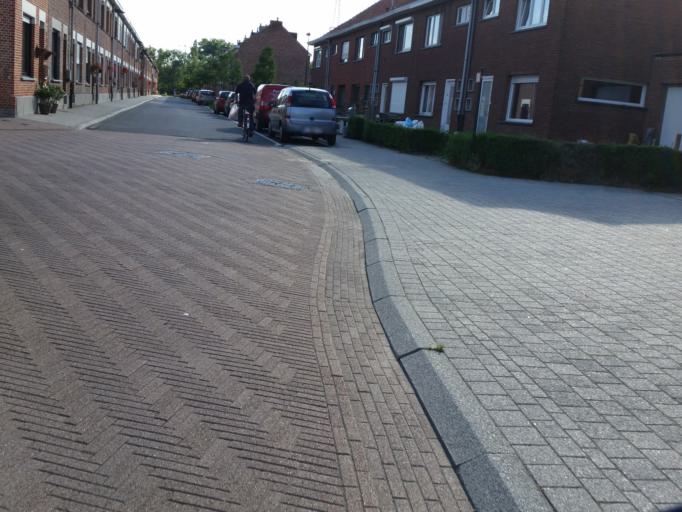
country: BE
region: Flanders
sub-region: Provincie Antwerpen
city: Mechelen
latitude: 51.0419
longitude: 4.4649
